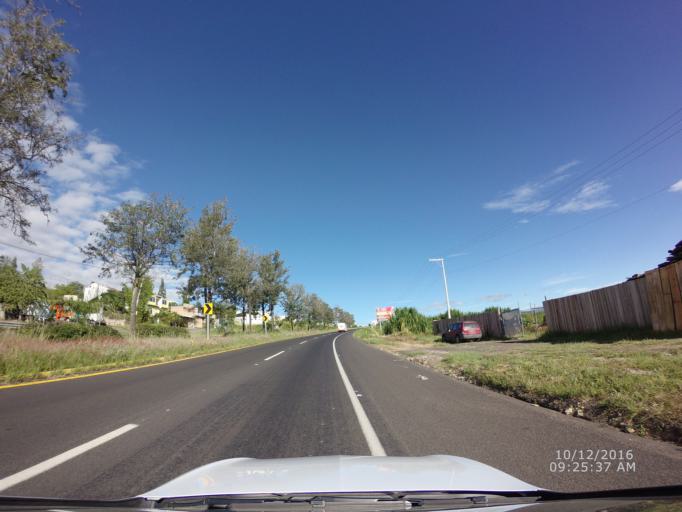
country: MX
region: Veracruz
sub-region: Emiliano Zapata
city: Dos Rios
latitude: 19.4931
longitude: -96.8169
